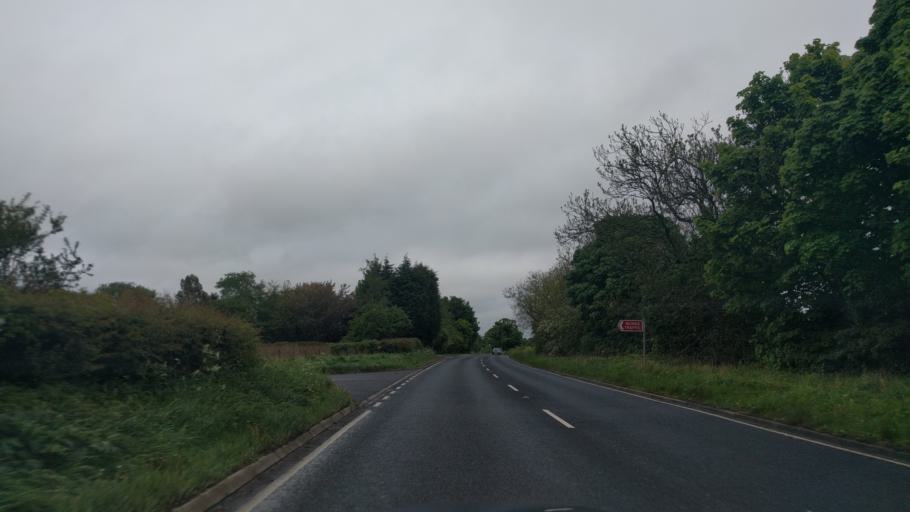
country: GB
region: England
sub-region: Northumberland
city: Pegswood
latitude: 55.1617
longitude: -1.6532
